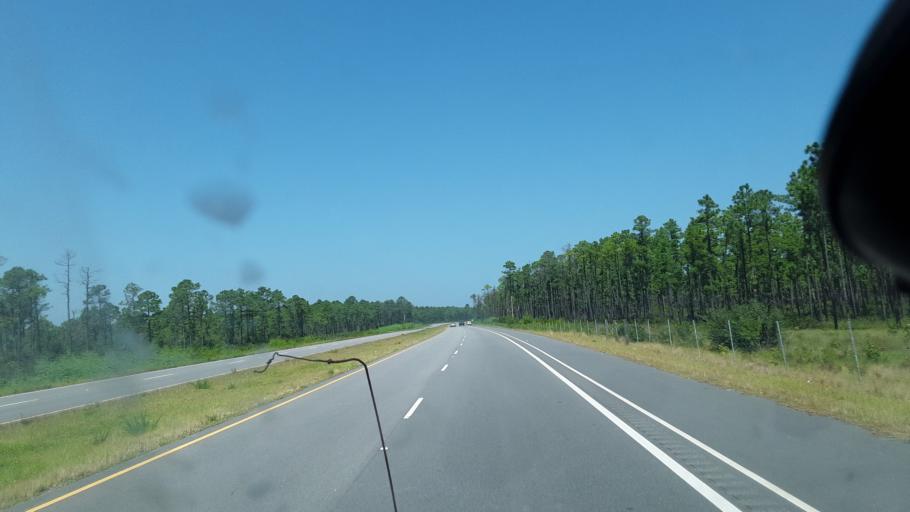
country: US
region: South Carolina
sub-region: Horry County
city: Myrtle Beach
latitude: 33.7880
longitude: -78.8791
